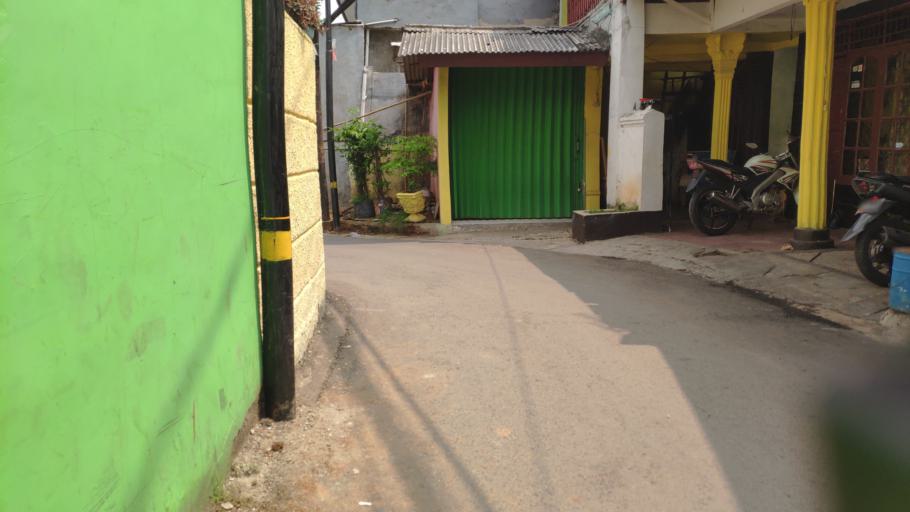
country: ID
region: West Java
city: Depok
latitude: -6.3081
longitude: 106.8366
